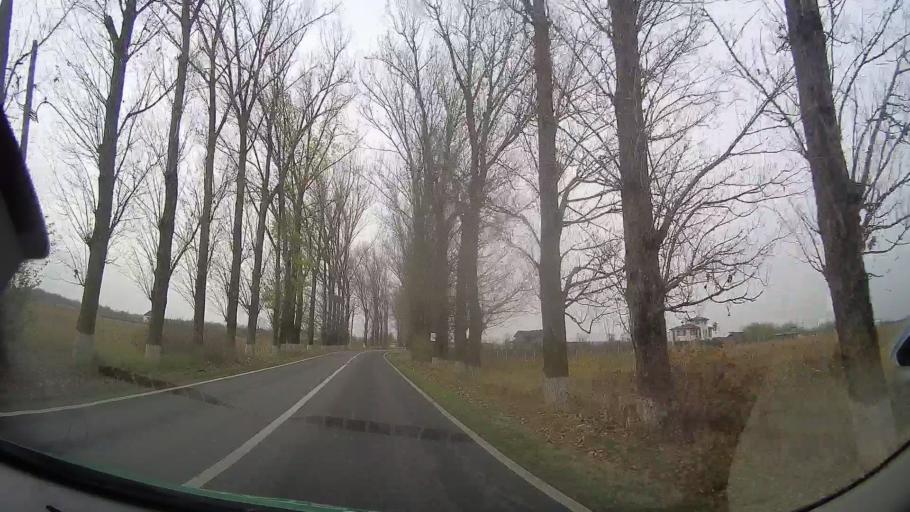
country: RO
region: Ilfov
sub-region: Comuna Gruiu
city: Silistea Snagovului
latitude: 44.7457
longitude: 26.2008
